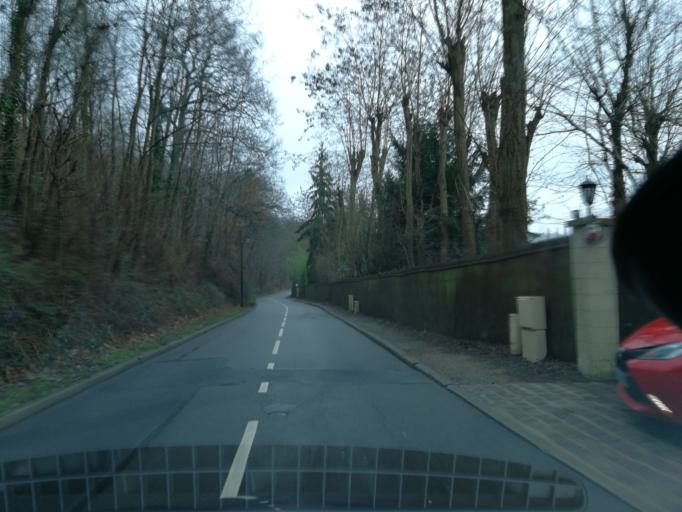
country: FR
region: Ile-de-France
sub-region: Departement des Yvelines
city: Les Loges-en-Josas
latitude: 48.7743
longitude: 2.1369
